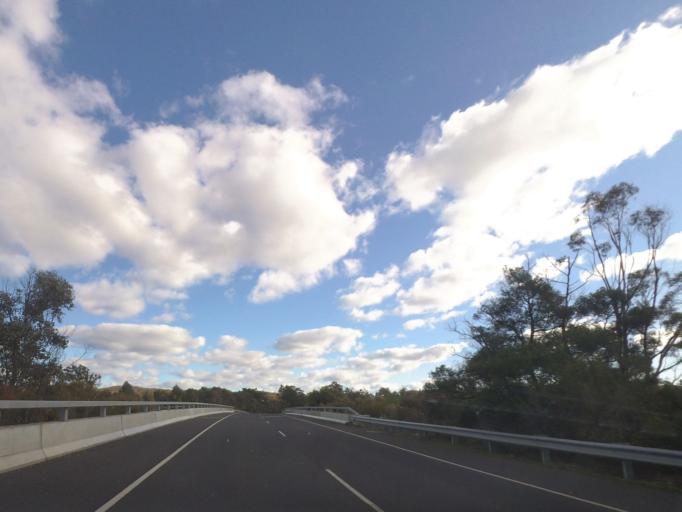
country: AU
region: Victoria
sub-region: Mount Alexander
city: Castlemaine
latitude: -37.1018
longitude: 144.3199
